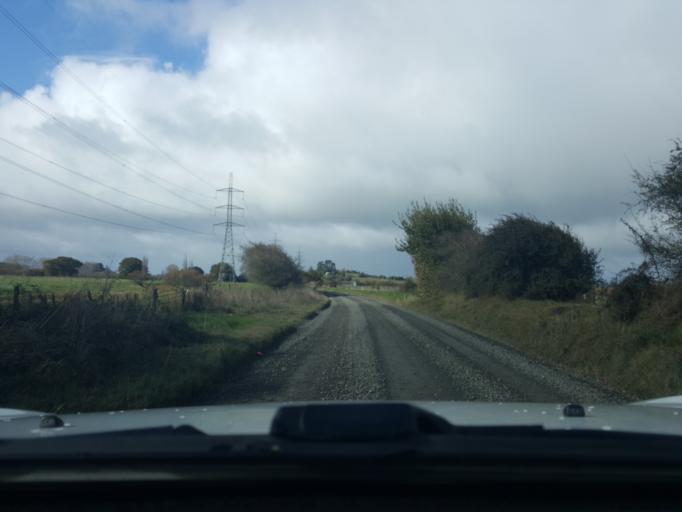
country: NZ
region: Waikato
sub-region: Waikato District
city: Te Kauwhata
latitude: -37.4169
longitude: 175.0668
